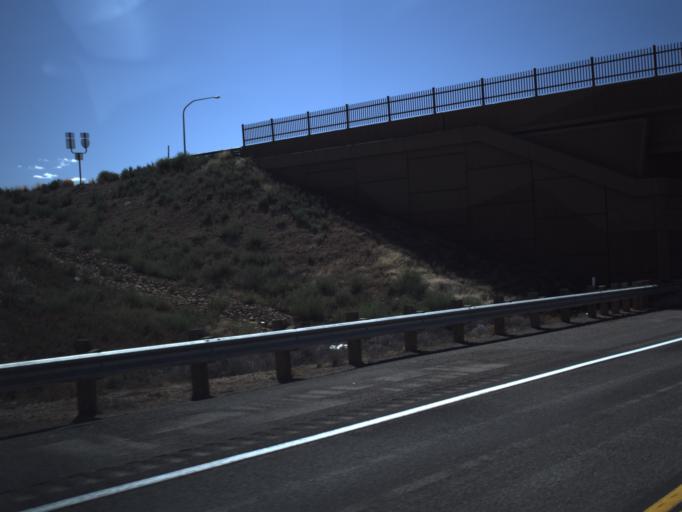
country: US
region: Utah
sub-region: Washington County
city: Washington
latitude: 37.0151
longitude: -113.4944
